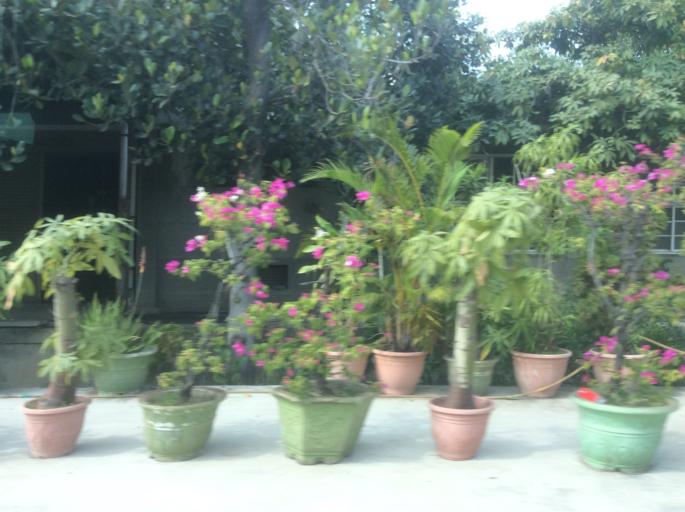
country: TW
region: Taiwan
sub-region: Tainan
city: Tainan
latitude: 22.9961
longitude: 120.2127
